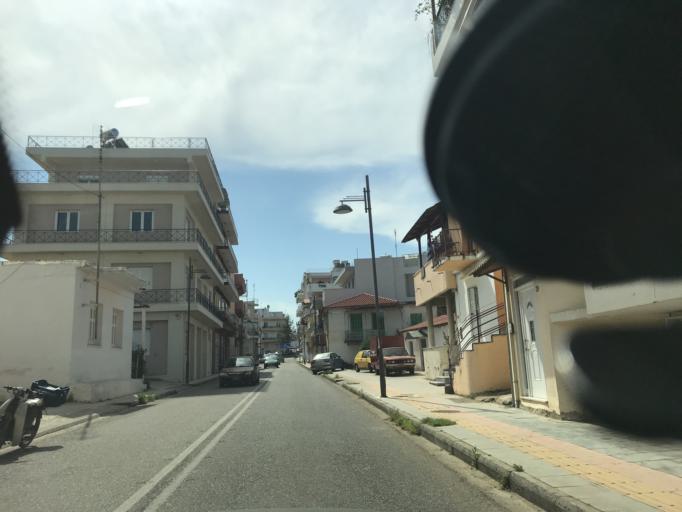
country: GR
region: West Greece
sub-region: Nomos Ileias
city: Pyrgos
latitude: 37.6761
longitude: 21.4416
